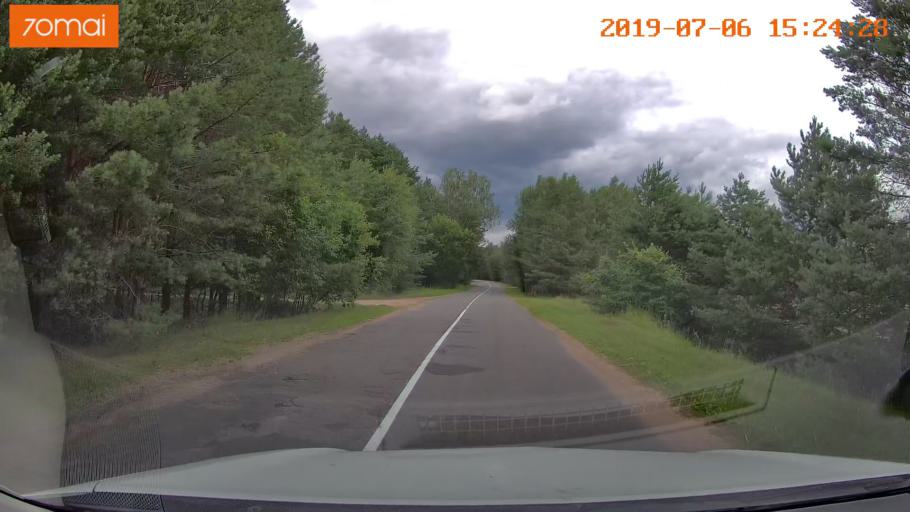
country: BY
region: Minsk
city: Valozhyn
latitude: 54.0200
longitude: 26.6026
